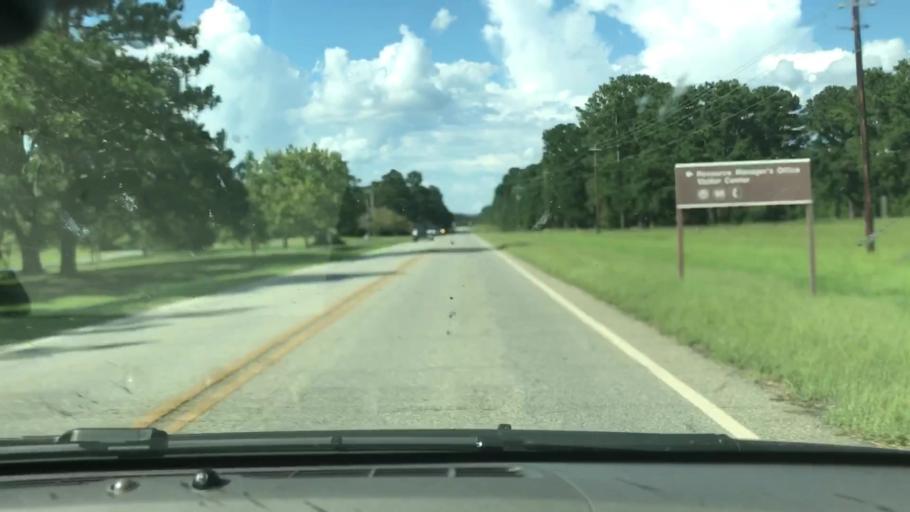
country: US
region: Georgia
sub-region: Clay County
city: Fort Gaines
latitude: 31.6341
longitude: -85.0442
